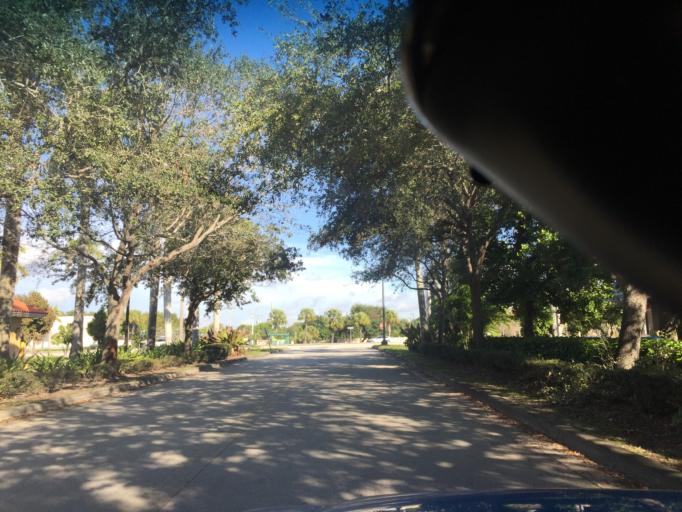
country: US
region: Florida
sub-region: Broward County
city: Pompano Beach
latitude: 26.2304
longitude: -80.1549
